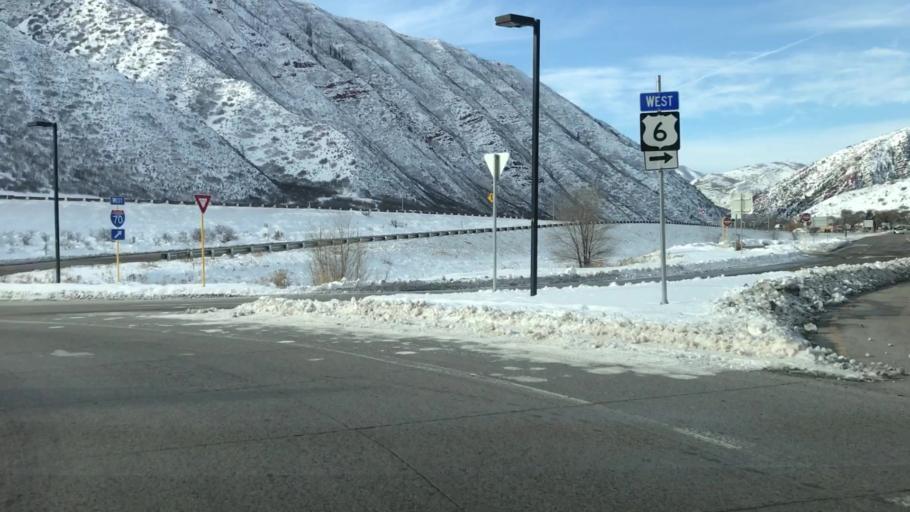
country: US
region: Colorado
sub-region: Garfield County
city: Glenwood Springs
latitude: 39.5616
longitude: -107.3614
